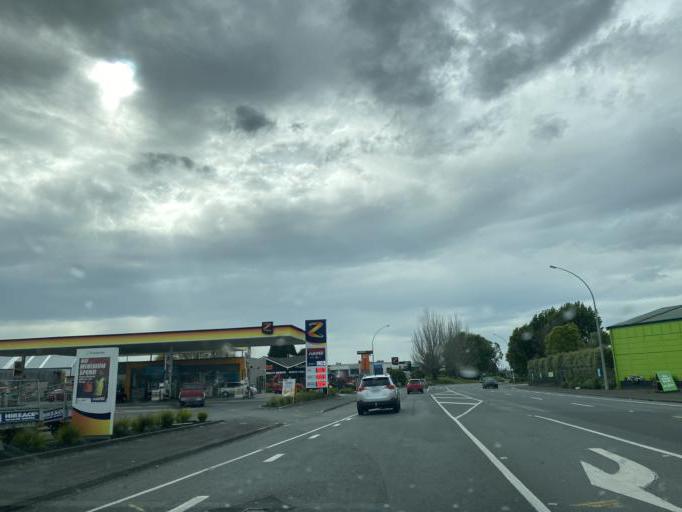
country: NZ
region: Waikato
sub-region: Hamilton City
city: Hamilton
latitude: -37.7864
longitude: 175.2564
